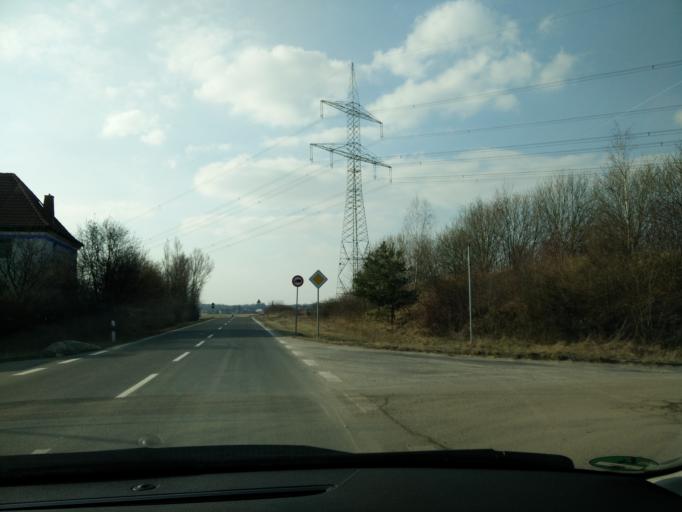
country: DE
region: Saxony
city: Konigsfeld
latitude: 51.0994
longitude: 12.7483
